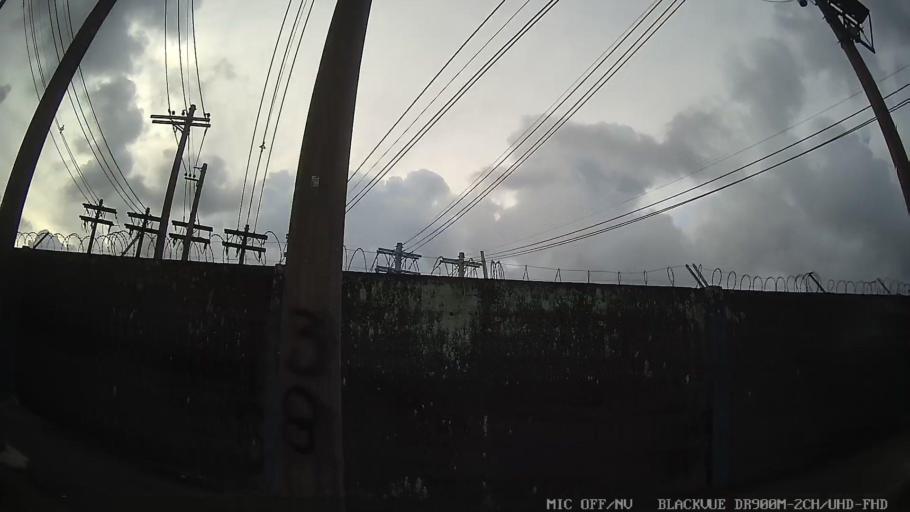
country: BR
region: Sao Paulo
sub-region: Itanhaem
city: Itanhaem
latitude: -24.1535
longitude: -46.7346
